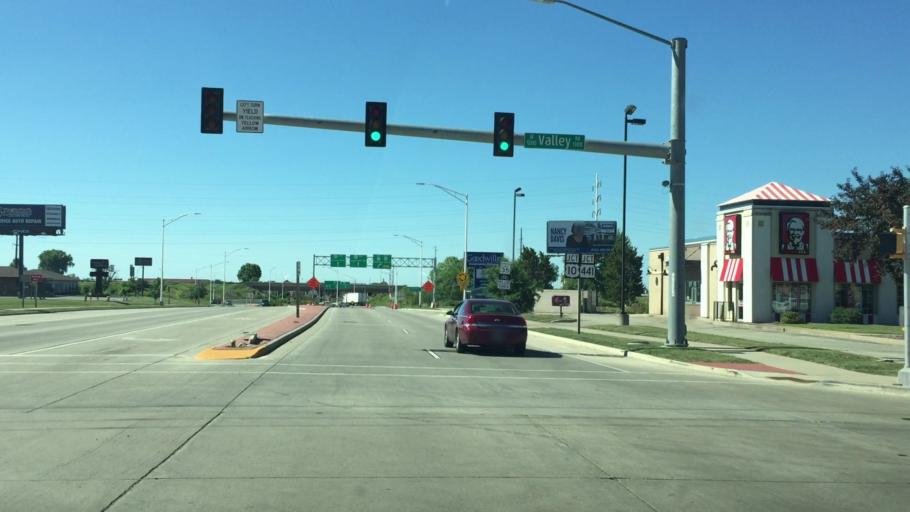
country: US
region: Wisconsin
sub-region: Outagamie County
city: Appleton
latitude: 44.2371
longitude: -88.4241
